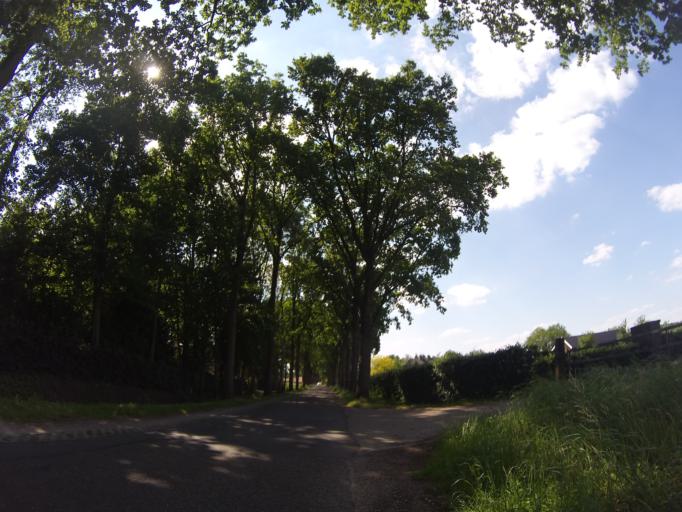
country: NL
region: Gelderland
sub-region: Gemeente Barneveld
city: Terschuur
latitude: 52.1444
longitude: 5.4940
